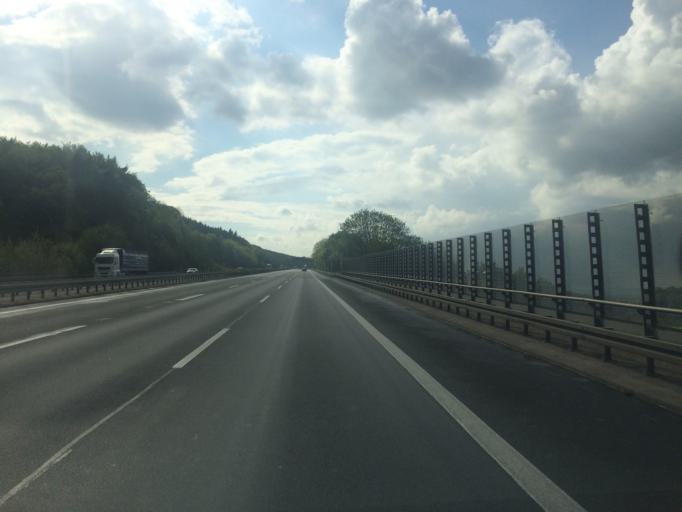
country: DE
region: Lower Saxony
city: Luhden
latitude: 52.2208
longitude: 9.0811
